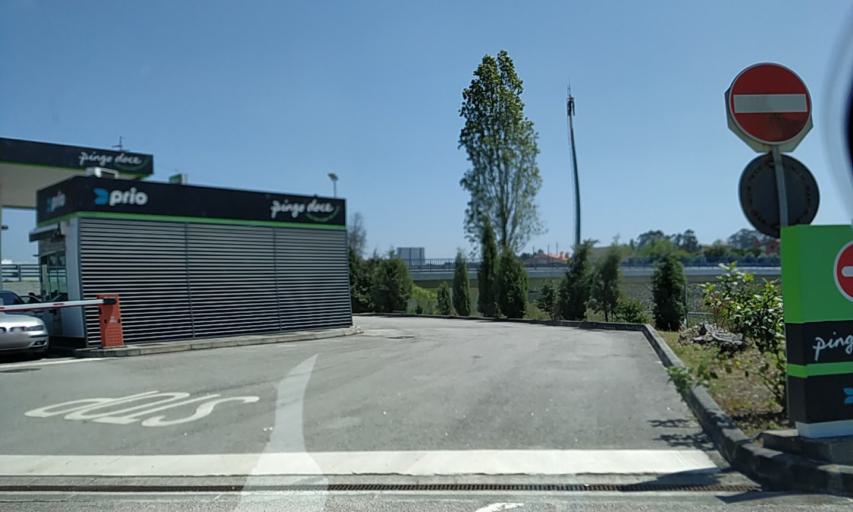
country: PT
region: Aveiro
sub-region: Aveiro
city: Aveiro
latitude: 40.6487
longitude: -8.6202
